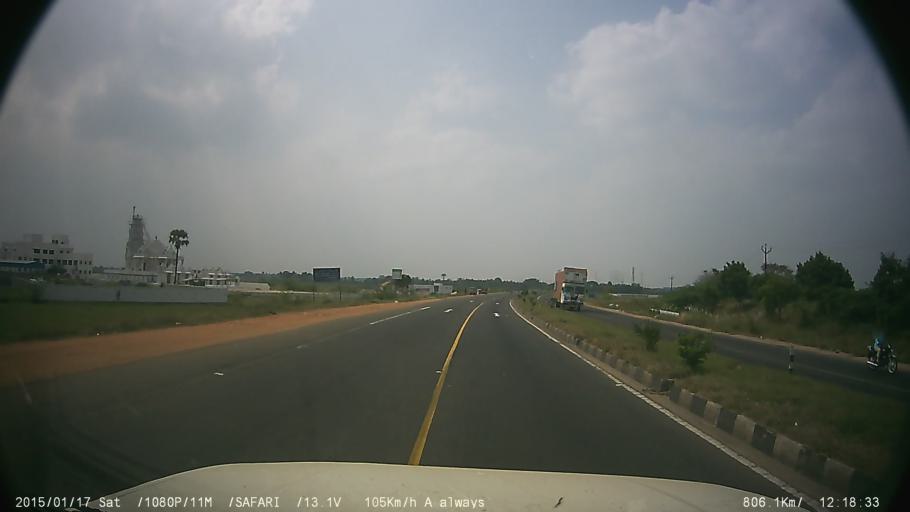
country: IN
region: Tamil Nadu
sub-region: Kancheepuram
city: Wallajahbad
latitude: 12.9057
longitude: 79.8268
